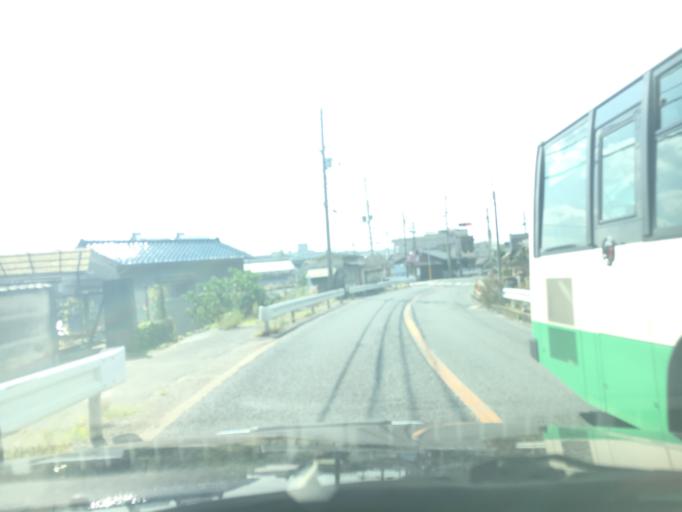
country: JP
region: Nara
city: Nara-shi
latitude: 34.6957
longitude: 135.8368
